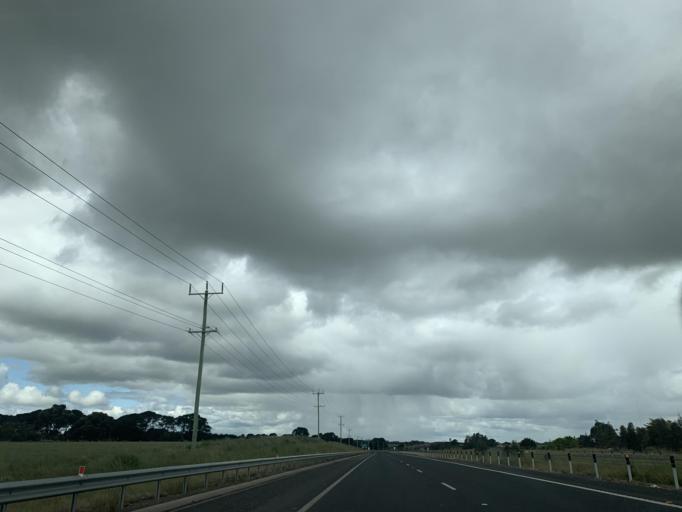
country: AU
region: Victoria
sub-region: Ballarat North
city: Newington
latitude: -37.4410
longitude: 143.4929
